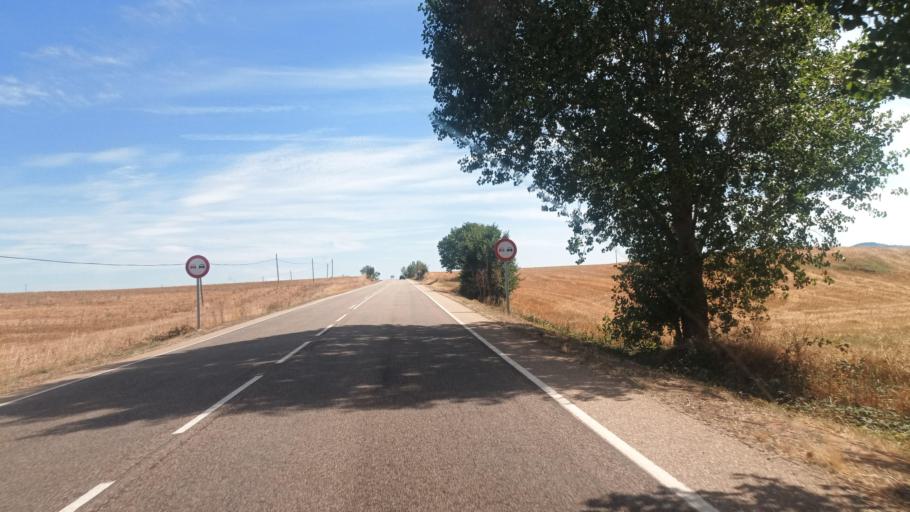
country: ES
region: Castille and Leon
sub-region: Provincia de Burgos
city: Quintanabureba
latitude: 42.6254
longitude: -3.3723
